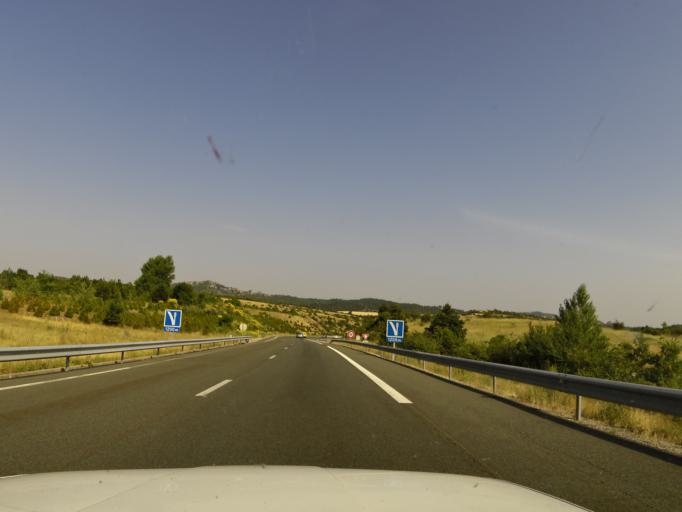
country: FR
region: Languedoc-Roussillon
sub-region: Departement de l'Herault
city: Lodeve
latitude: 43.8465
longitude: 3.3083
